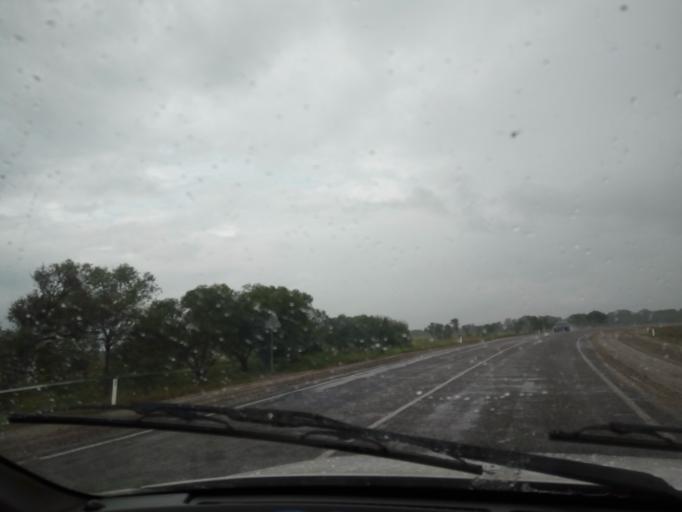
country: RU
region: Primorskiy
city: Dal'nerechensk
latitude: 45.9012
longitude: 133.7393
